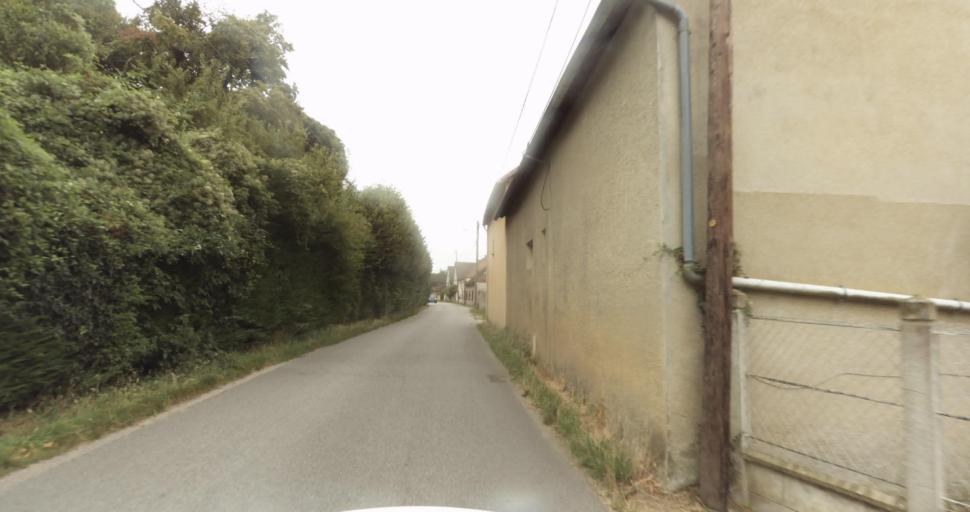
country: FR
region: Haute-Normandie
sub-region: Departement de l'Eure
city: Saint-Germain-sur-Avre
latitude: 48.7622
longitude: 1.2618
